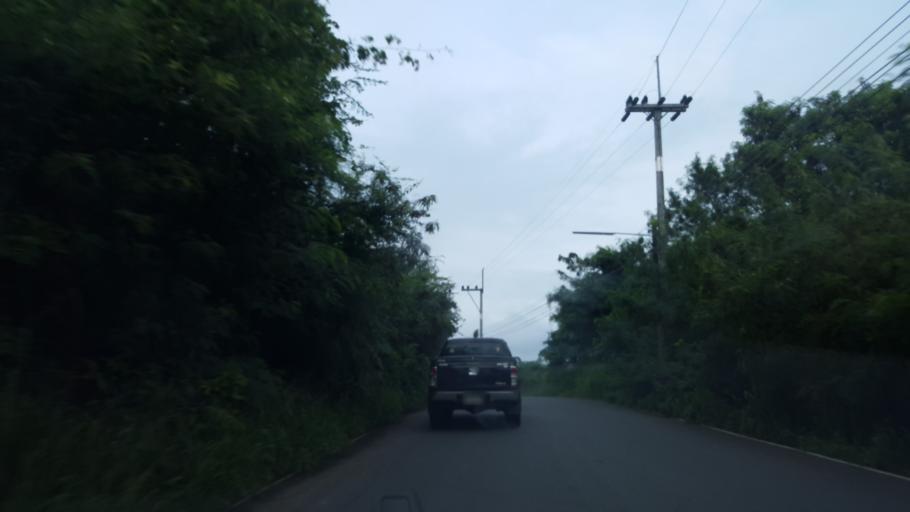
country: TH
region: Chon Buri
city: Sattahip
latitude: 12.6965
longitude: 100.9068
